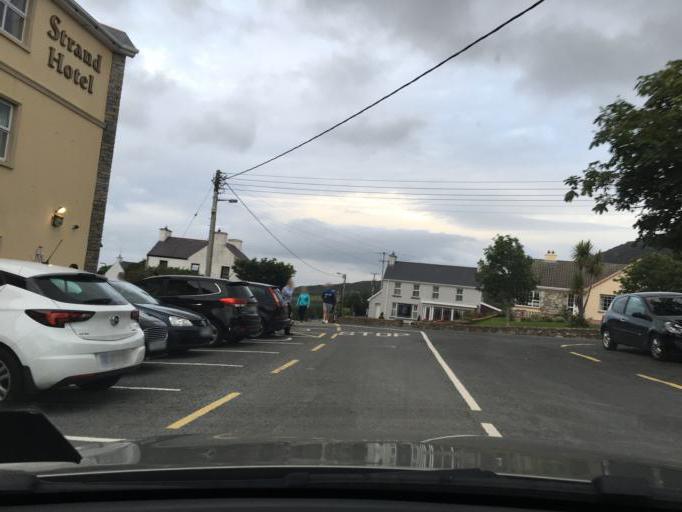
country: IE
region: Ulster
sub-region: County Donegal
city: Carndonagh
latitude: 55.2807
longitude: -7.3933
